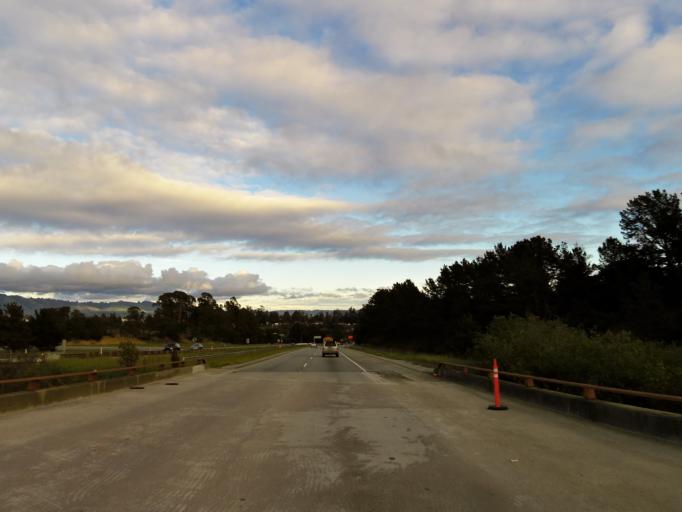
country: US
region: California
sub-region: Santa Cruz County
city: Aptos Hills-Larkin Valley
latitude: 36.9314
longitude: -121.8109
